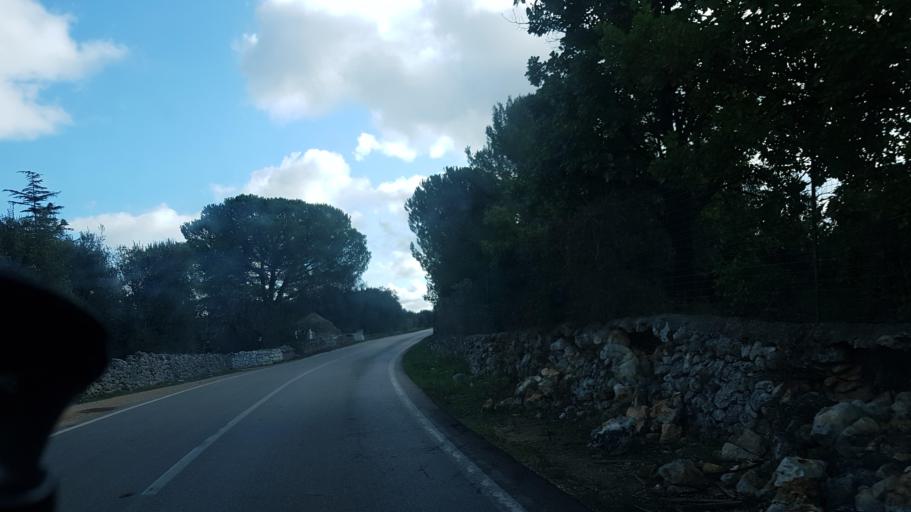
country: IT
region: Apulia
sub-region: Provincia di Brindisi
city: Ostuni
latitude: 40.6783
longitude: 17.5917
